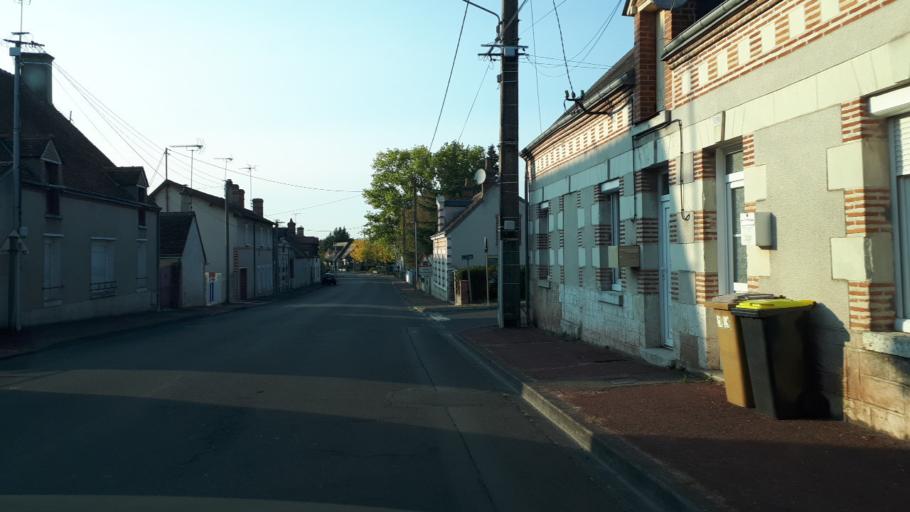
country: FR
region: Centre
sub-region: Departement du Loir-et-Cher
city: Romorantin-Lanthenay
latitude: 47.3626
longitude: 1.7331
